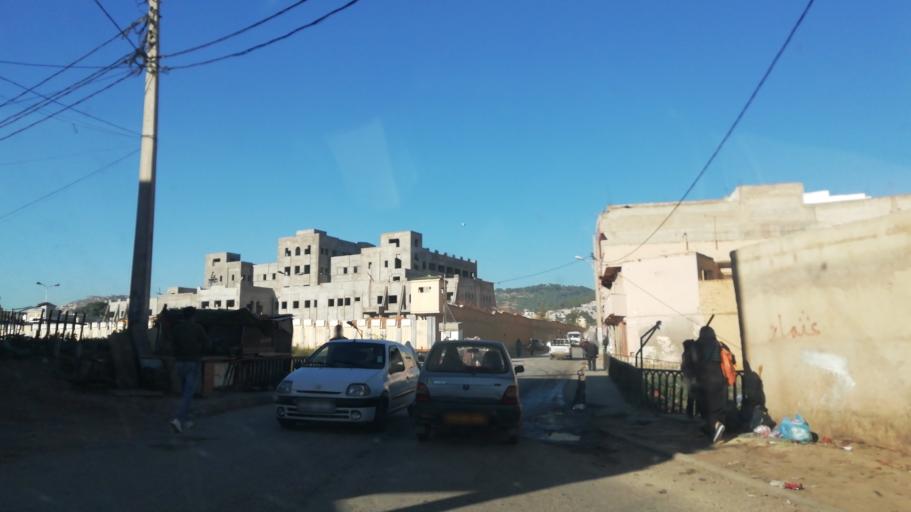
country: DZ
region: Oran
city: Oran
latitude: 35.6858
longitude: -0.6697
